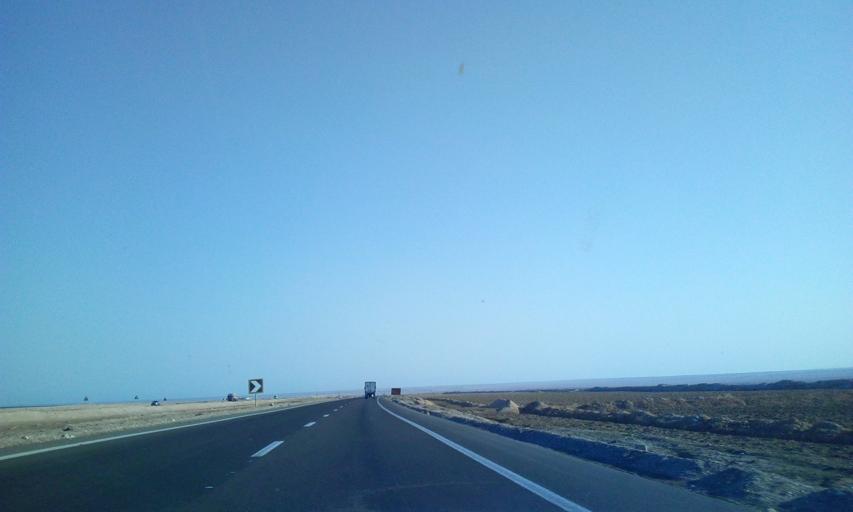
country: EG
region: South Sinai
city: Tor
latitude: 28.6245
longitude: 32.8597
